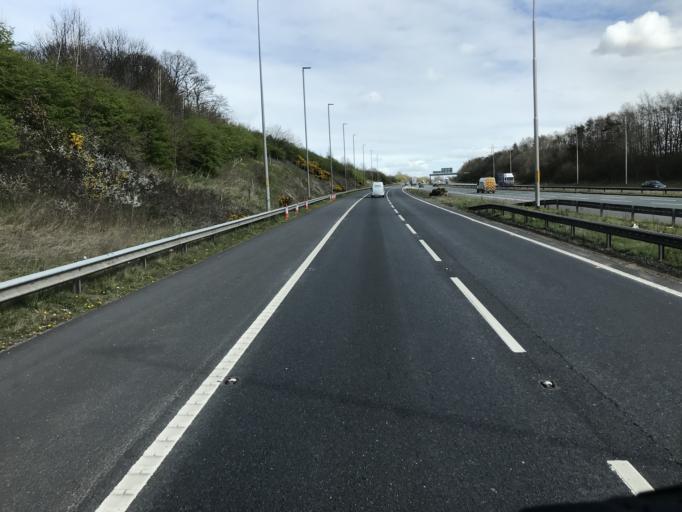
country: GB
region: England
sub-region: Knowsley
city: Whiston
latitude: 53.4008
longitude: -2.8007
